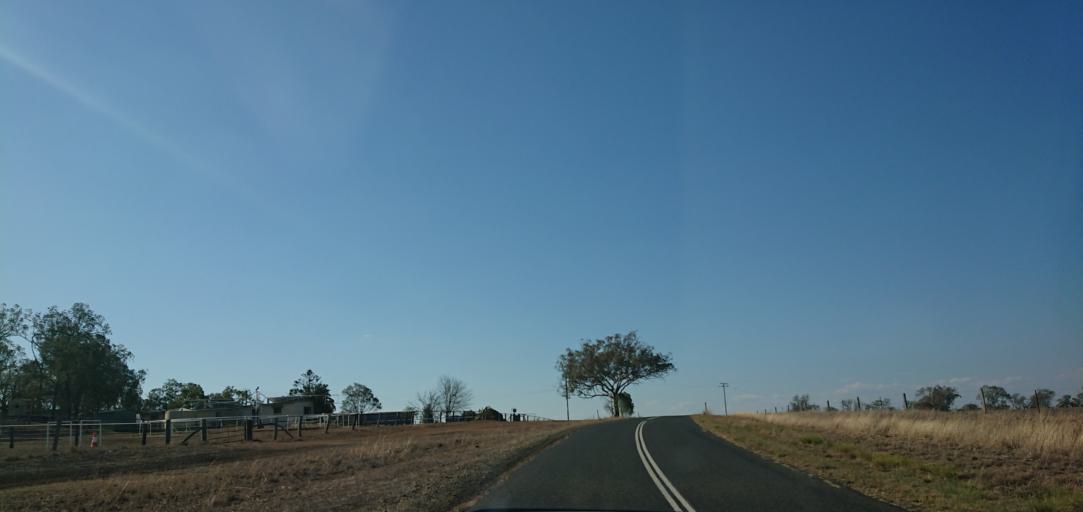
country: AU
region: Queensland
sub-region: Toowoomba
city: Westbrook
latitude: -27.7183
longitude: 151.7198
